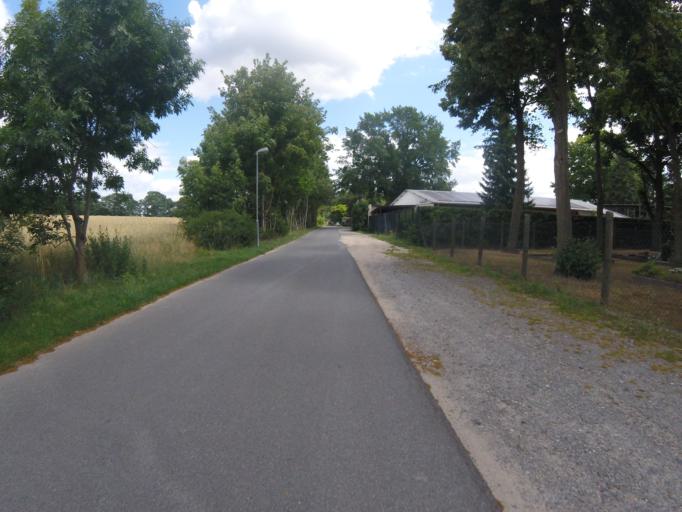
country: DE
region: Brandenburg
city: Bestensee
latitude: 52.2438
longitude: 13.6193
